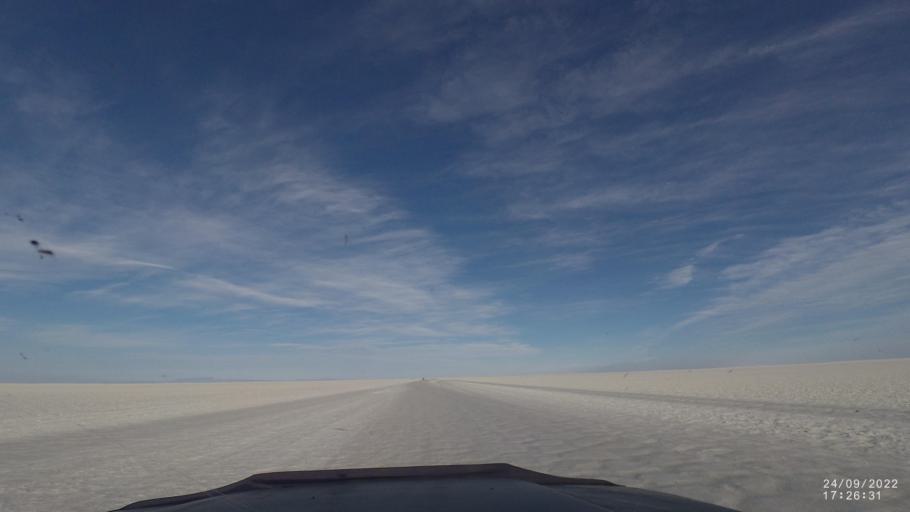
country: BO
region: Potosi
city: Colchani
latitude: -20.2952
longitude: -67.4671
